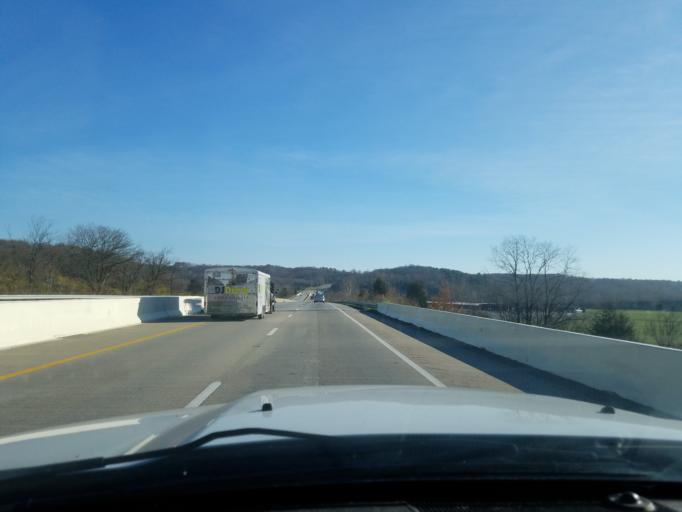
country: US
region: Ohio
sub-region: Clermont County
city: Batavia
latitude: 39.0844
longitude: -84.1863
